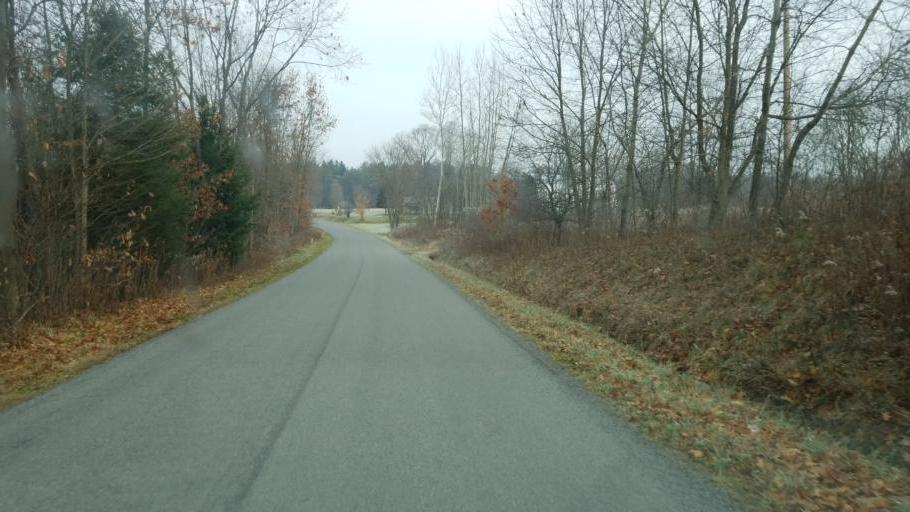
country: US
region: Pennsylvania
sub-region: Crawford County
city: Cochranton
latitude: 41.5169
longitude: -80.1212
